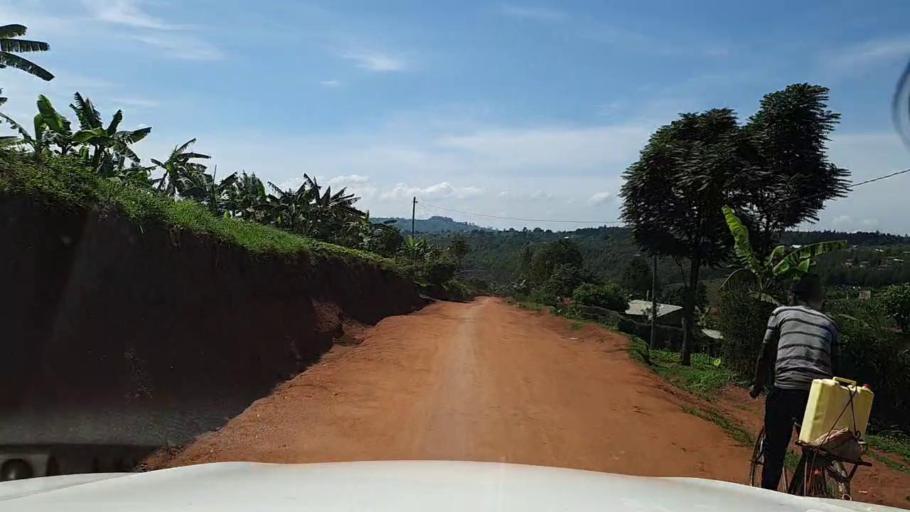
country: RW
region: Southern Province
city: Butare
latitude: -2.6961
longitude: 29.8544
